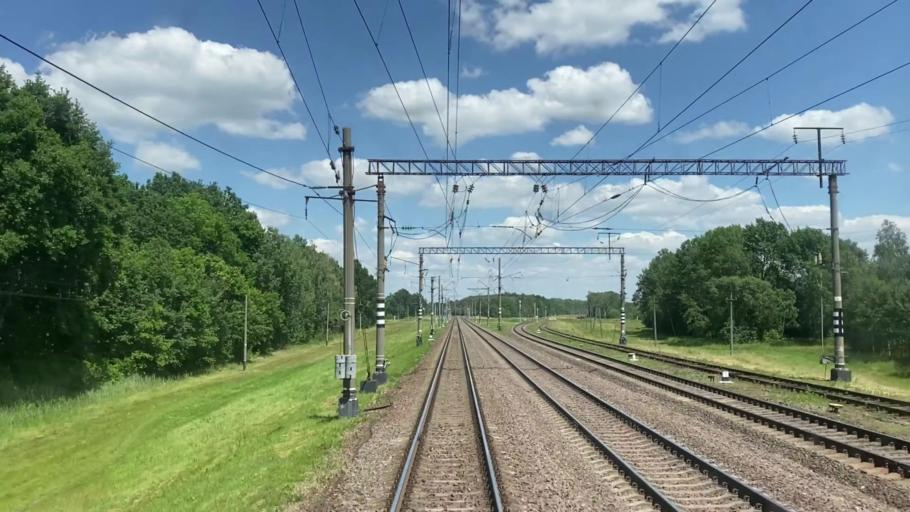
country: BY
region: Brest
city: Zhabinka
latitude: 52.2108
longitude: 24.0416
